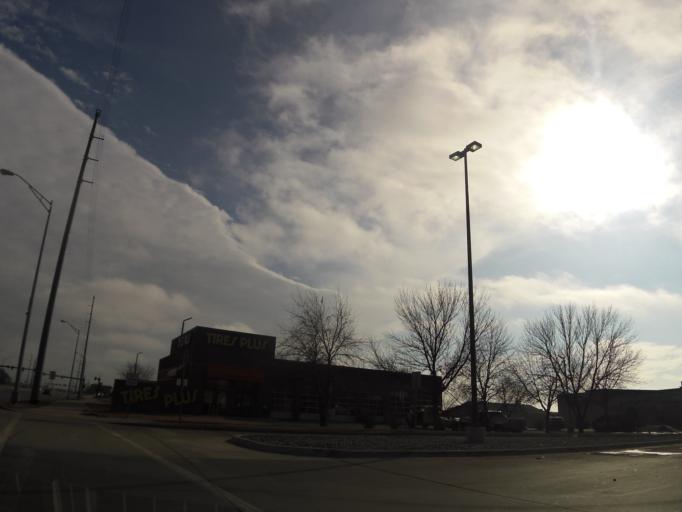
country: US
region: North Dakota
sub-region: Grand Forks County
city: Grand Forks
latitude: 47.8877
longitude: -97.0670
